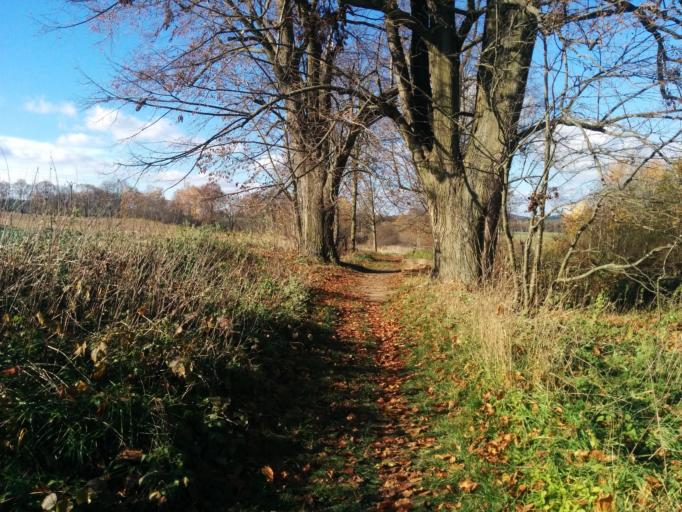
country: CZ
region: Vysocina
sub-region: Okres Jihlava
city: Jihlava
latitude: 49.4107
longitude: 15.5534
